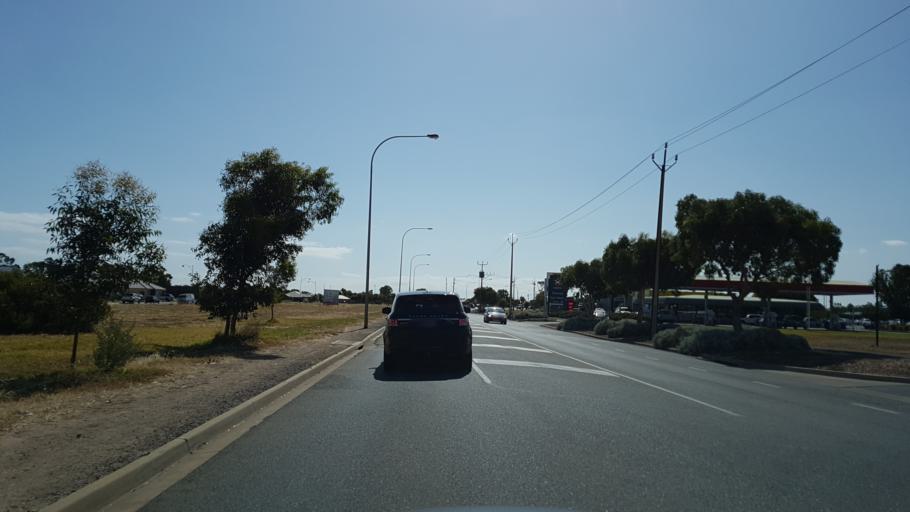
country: AU
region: South Australia
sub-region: Onkaparinga
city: Port Willunga
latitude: -35.2789
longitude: 138.4618
